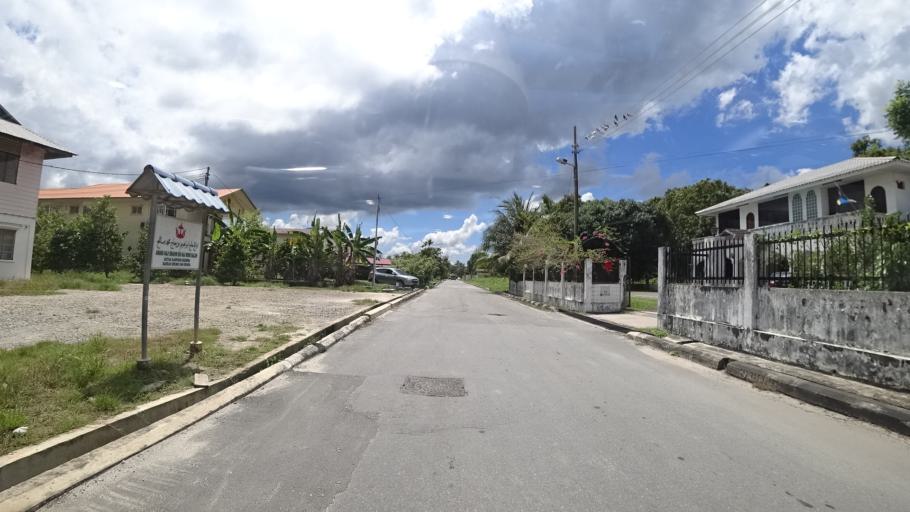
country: BN
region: Brunei and Muara
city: Bandar Seri Begawan
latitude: 4.8561
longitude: 114.8949
